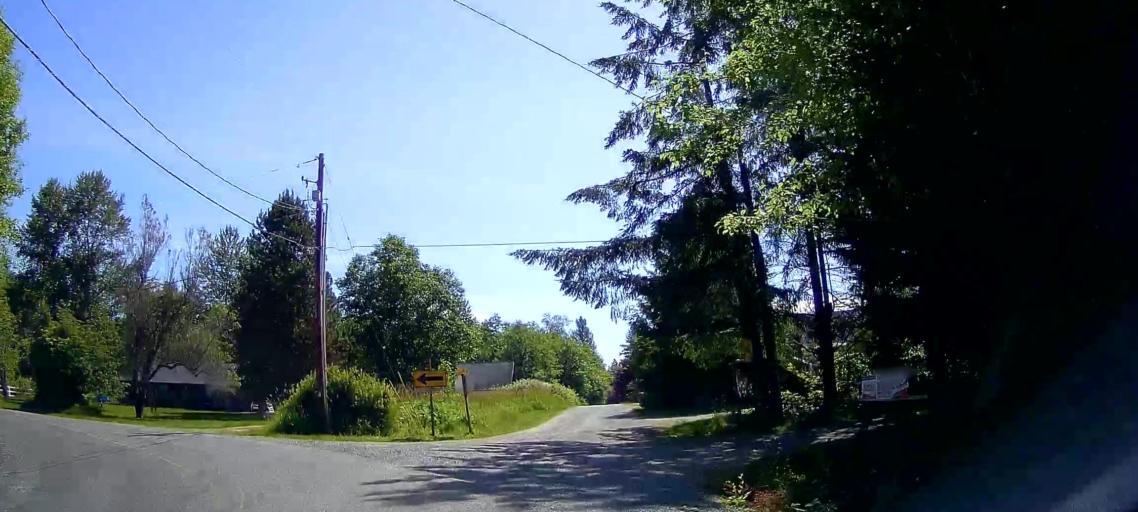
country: US
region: Washington
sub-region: Skagit County
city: Sedro-Woolley
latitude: 48.5549
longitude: -122.2688
